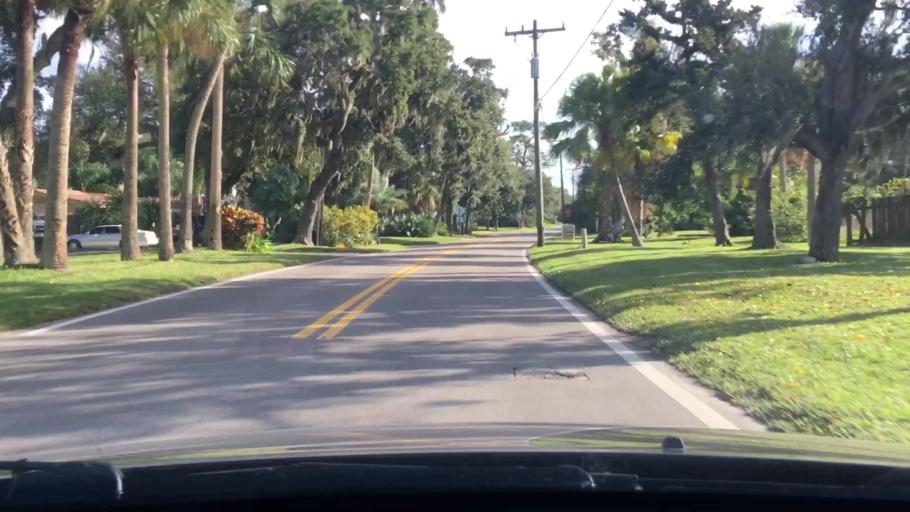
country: US
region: Florida
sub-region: Volusia County
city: Ormond Beach
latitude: 29.3164
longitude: -81.0602
